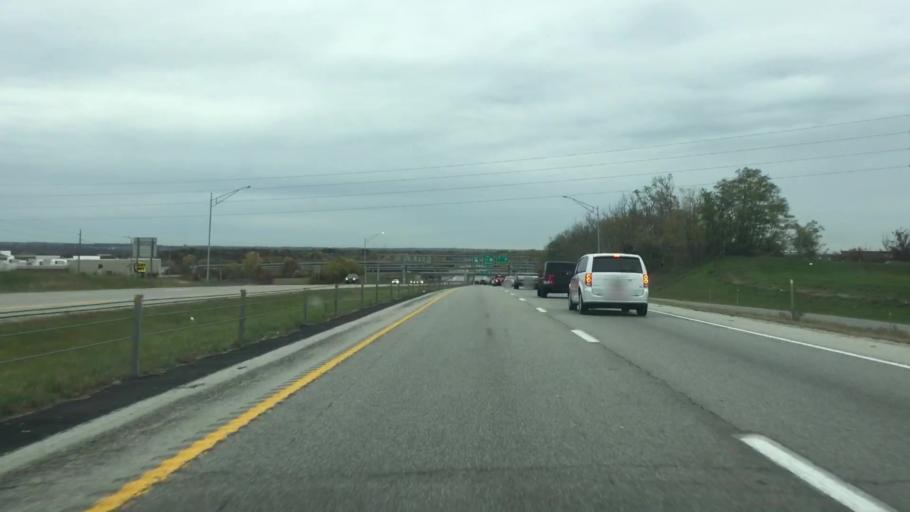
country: US
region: Missouri
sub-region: Jackson County
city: Lees Summit
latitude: 38.9277
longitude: -94.4044
